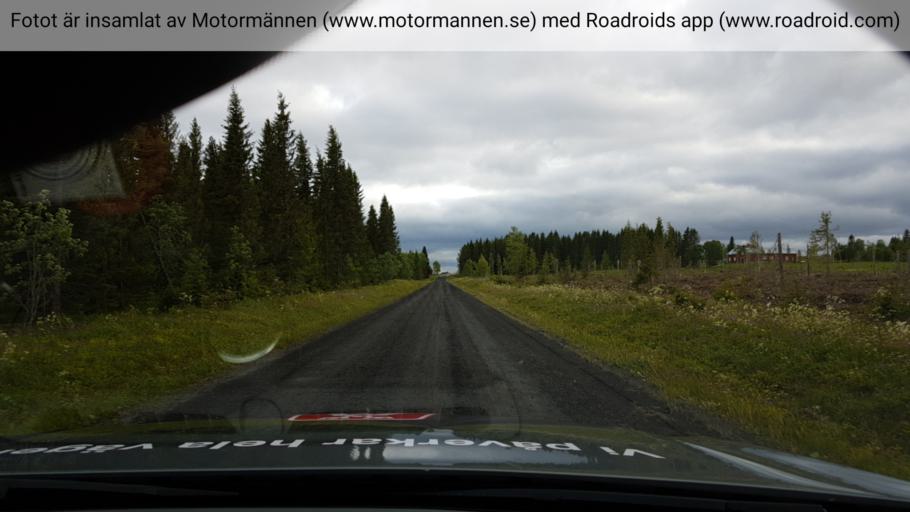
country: SE
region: Jaemtland
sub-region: OEstersunds Kommun
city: Lit
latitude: 63.6182
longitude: 15.0099
